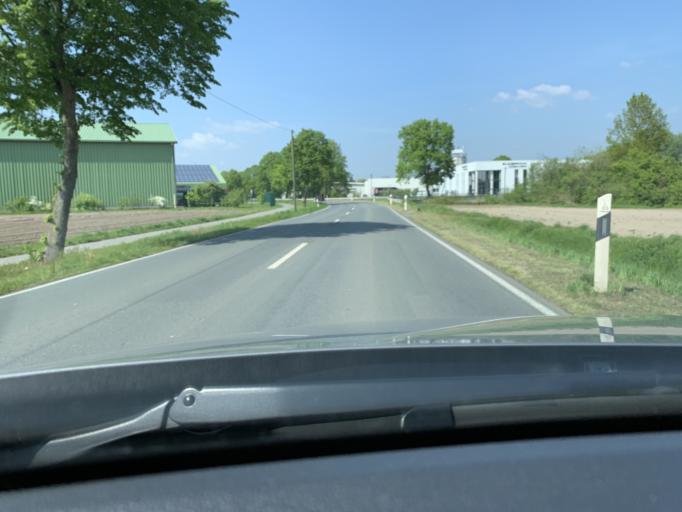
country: DE
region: North Rhine-Westphalia
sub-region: Regierungsbezirk Detmold
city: Langenberg
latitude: 51.7952
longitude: 8.3704
